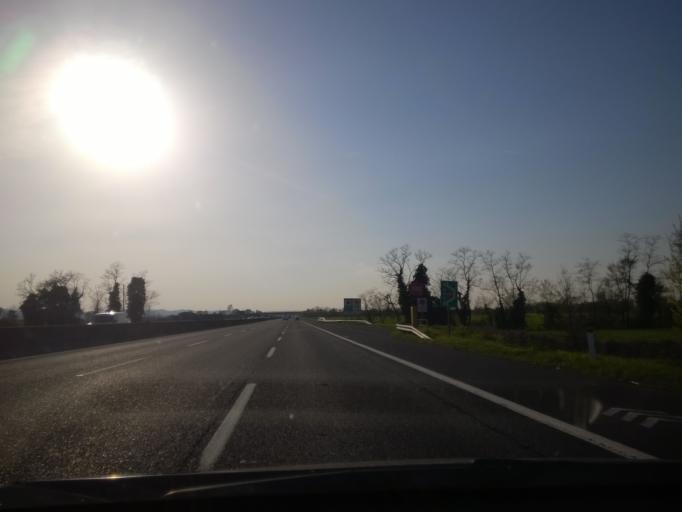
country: IT
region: Emilia-Romagna
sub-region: Provincia di Bologna
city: Castel Guelfo di Bologna
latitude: 44.4124
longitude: 11.6507
